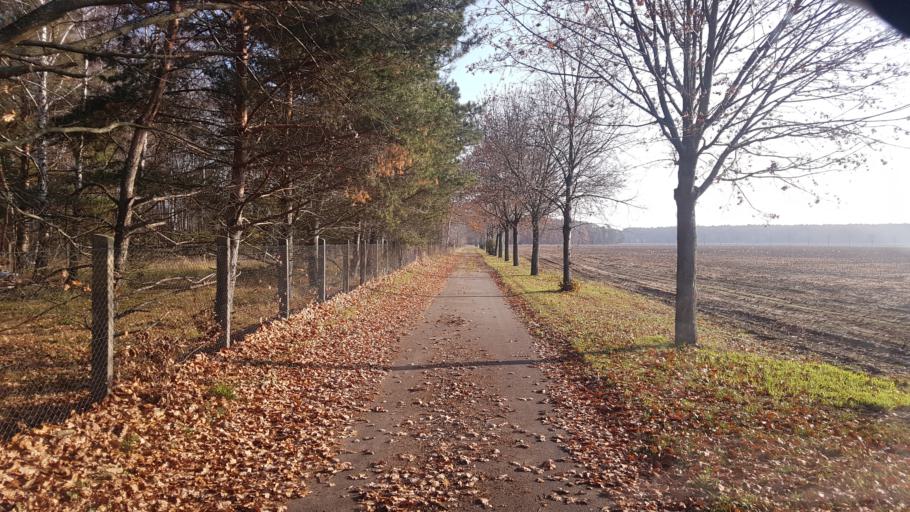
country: DE
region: Brandenburg
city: Tettau
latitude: 51.4358
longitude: 13.7346
